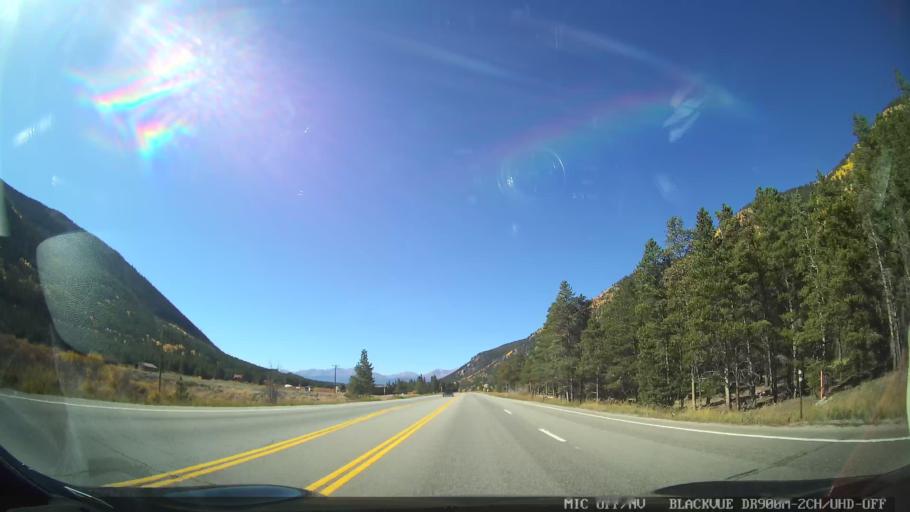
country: US
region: Colorado
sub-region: Lake County
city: Leadville North
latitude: 39.3037
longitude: -106.2603
